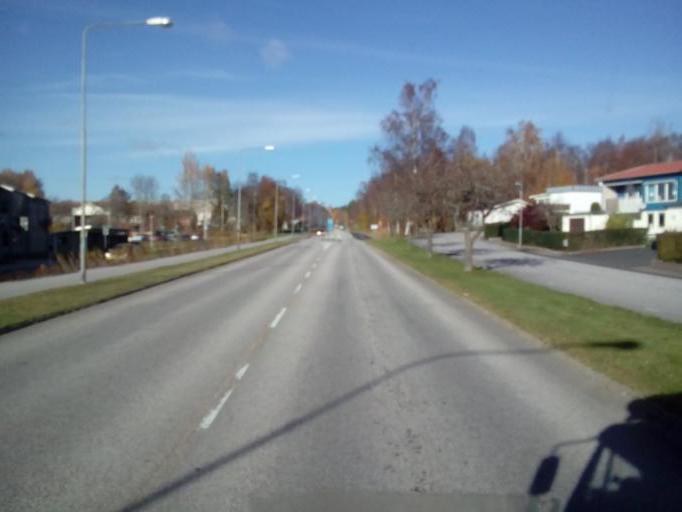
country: SE
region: Kalmar
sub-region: Vimmerby Kommun
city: Vimmerby
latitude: 57.6656
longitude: 15.8755
